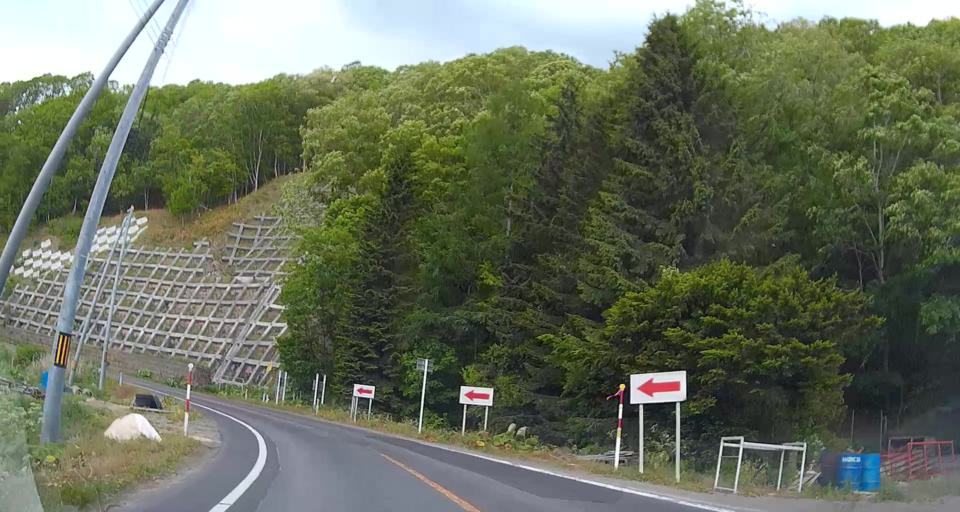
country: JP
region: Hokkaido
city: Chitose
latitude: 42.7606
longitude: 141.9504
